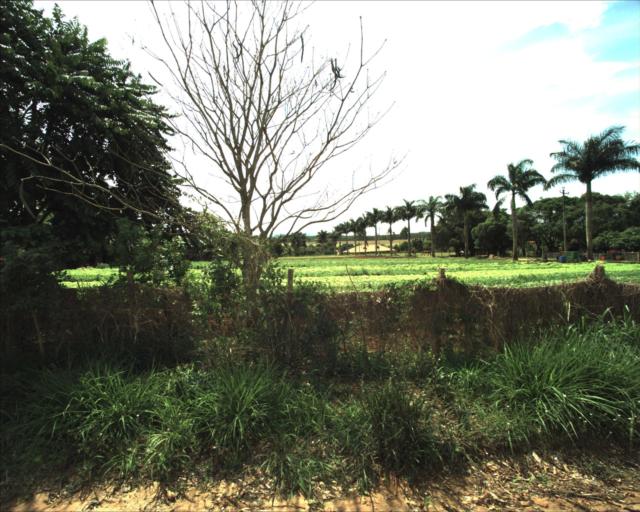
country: BR
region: Sao Paulo
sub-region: Aracoiaba Da Serra
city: Aracoiaba da Serra
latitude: -23.5540
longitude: -47.5490
